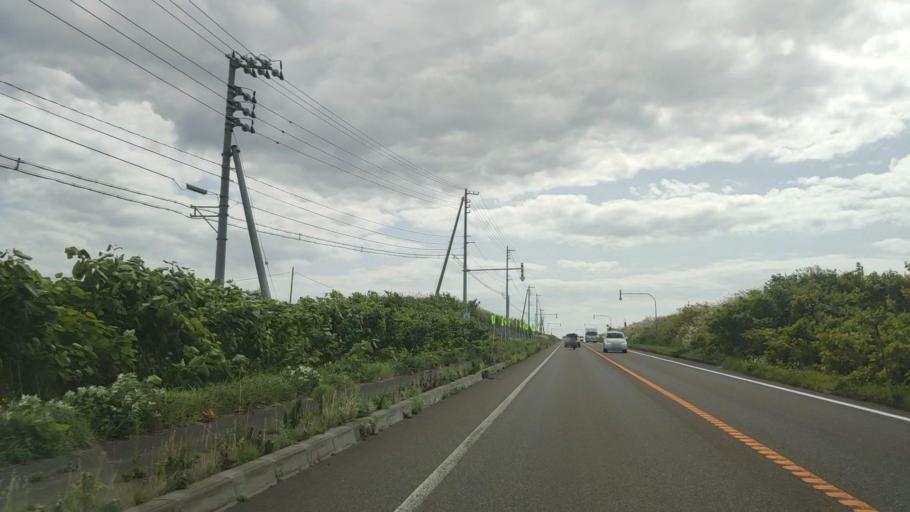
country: JP
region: Hokkaido
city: Rumoi
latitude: 44.5275
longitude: 141.7660
